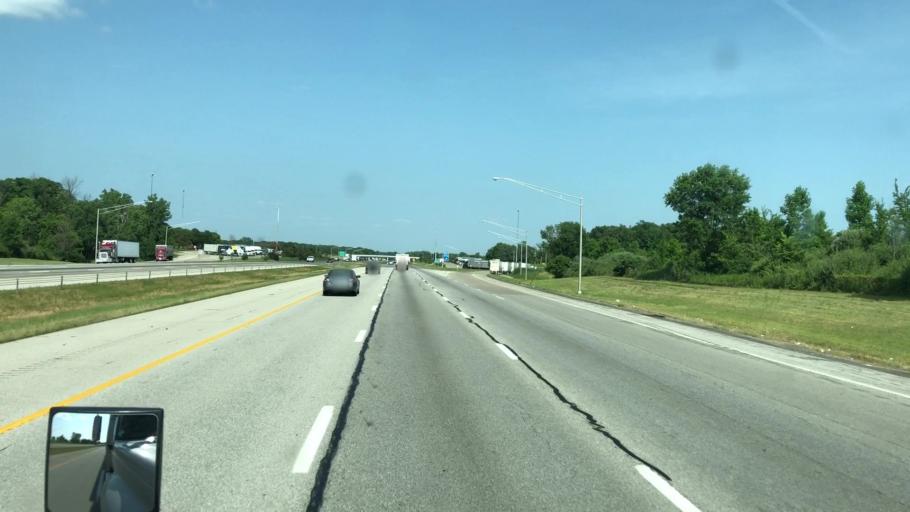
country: US
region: Ohio
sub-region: Madison County
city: Choctaw Lake
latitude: 39.9398
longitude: -83.5368
